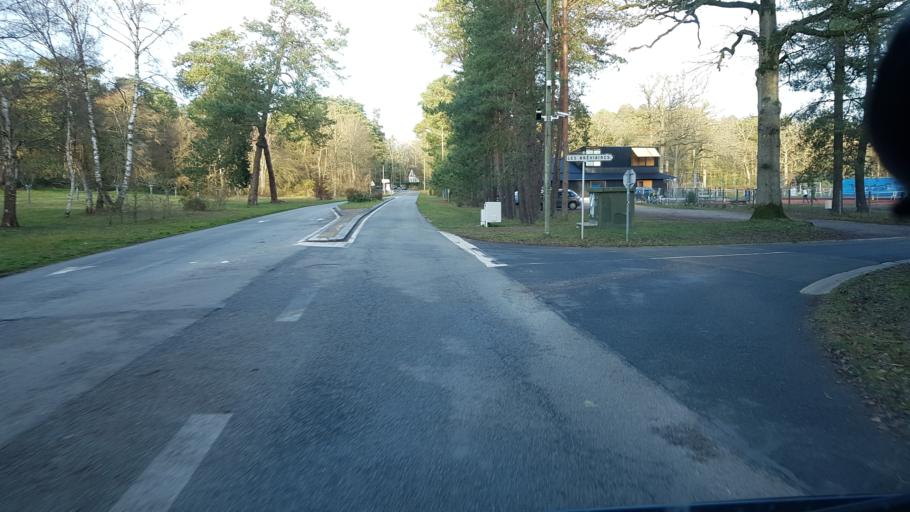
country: FR
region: Ile-de-France
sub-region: Departement des Yvelines
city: Saint-Leger-en-Yvelines
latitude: 48.6873
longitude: 1.7665
